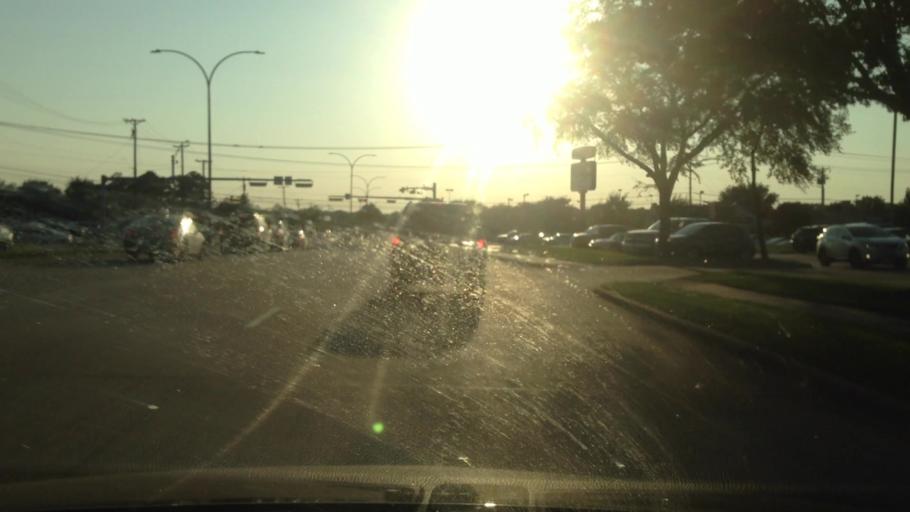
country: US
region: Texas
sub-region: Tarrant County
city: Dalworthington Gardens
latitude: 32.6490
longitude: -97.1339
